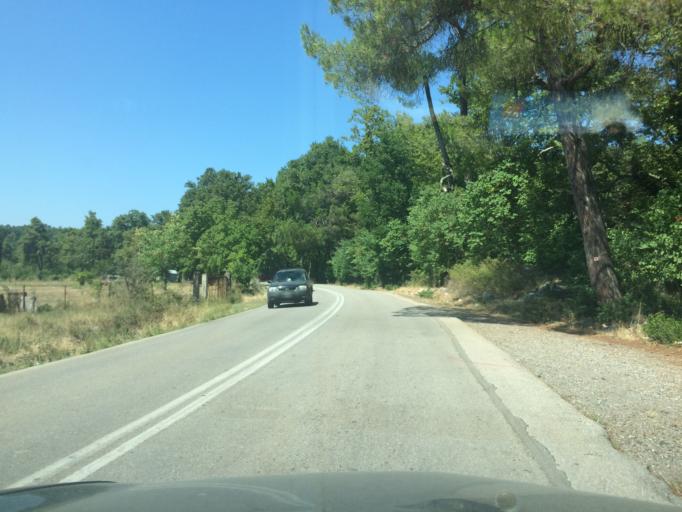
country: GR
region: Central Greece
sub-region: Nomos Evvoias
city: Prokopion
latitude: 38.7181
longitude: 23.5172
